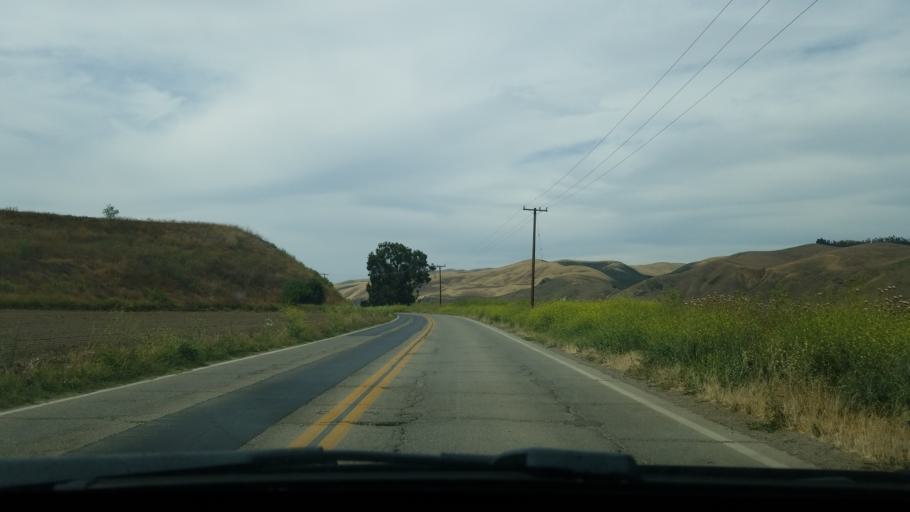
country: US
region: California
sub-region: Santa Barbara County
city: Orcutt
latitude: 34.9026
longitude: -120.3167
